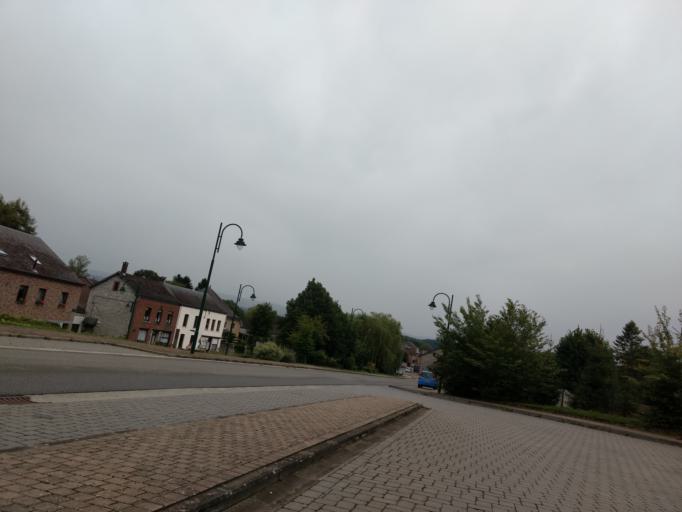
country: BE
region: Wallonia
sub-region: Province du Luxembourg
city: Hotton
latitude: 50.2835
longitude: 5.4406
